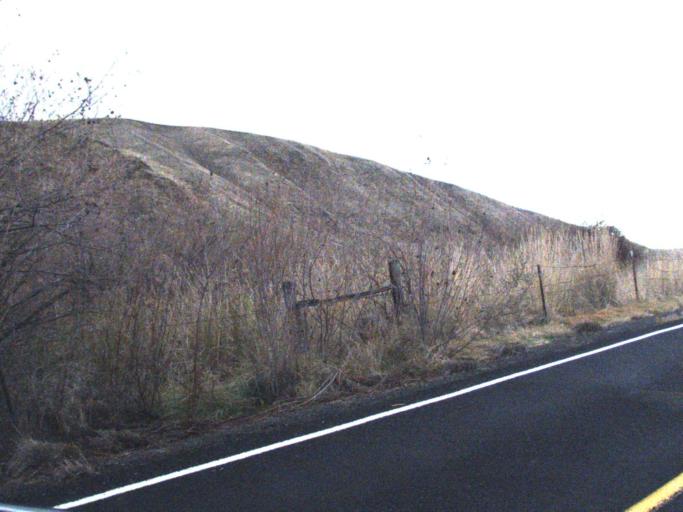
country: US
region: Washington
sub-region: Columbia County
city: Dayton
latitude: 46.5063
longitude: -118.0714
